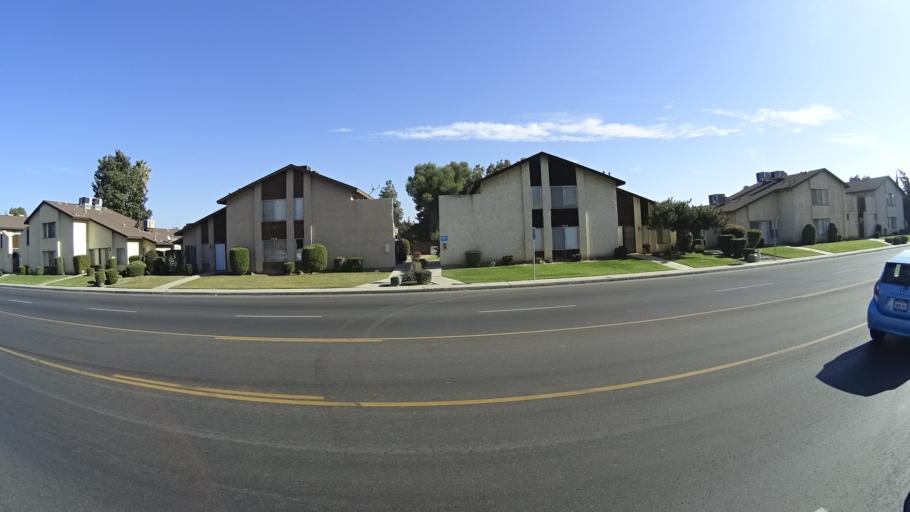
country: US
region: California
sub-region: Kern County
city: Greenacres
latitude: 35.3308
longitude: -119.0746
